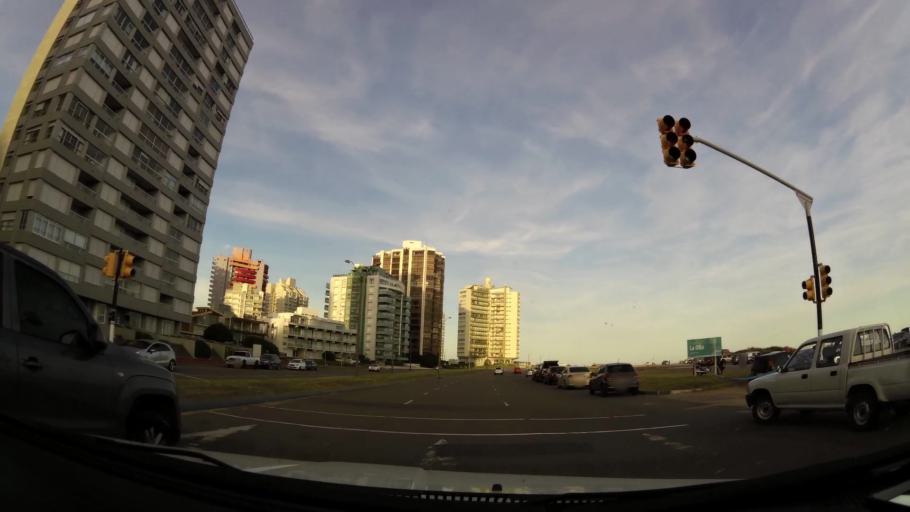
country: UY
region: Maldonado
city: Punta del Este
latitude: -34.9546
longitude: -54.9339
